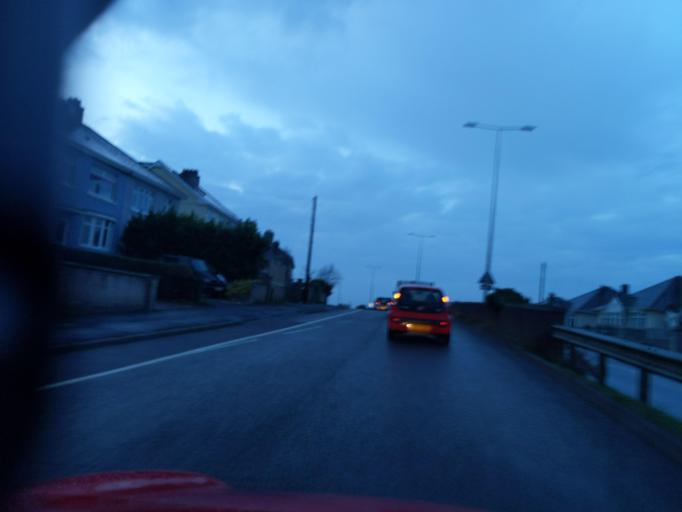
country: GB
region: England
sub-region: Plymouth
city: Plymstock
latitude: 50.3619
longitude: -4.0668
